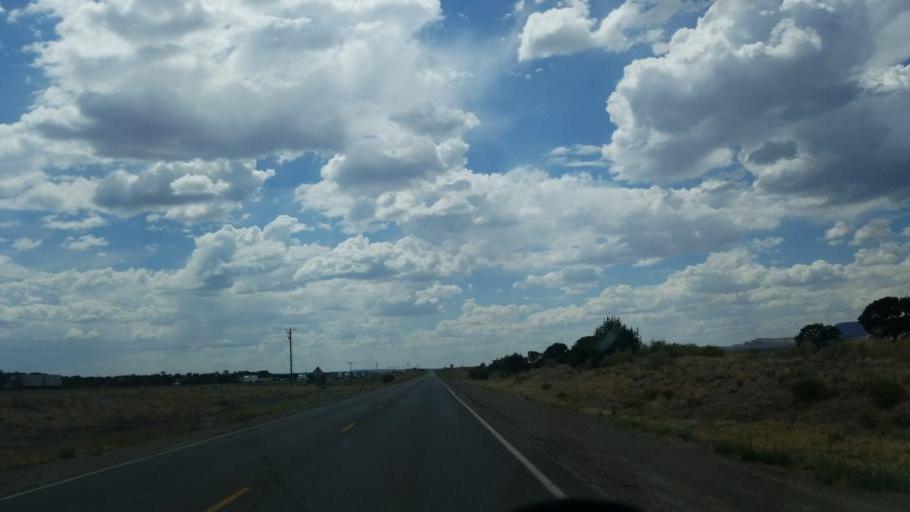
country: US
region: New Mexico
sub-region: McKinley County
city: Thoreau
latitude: 35.3866
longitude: -108.1467
